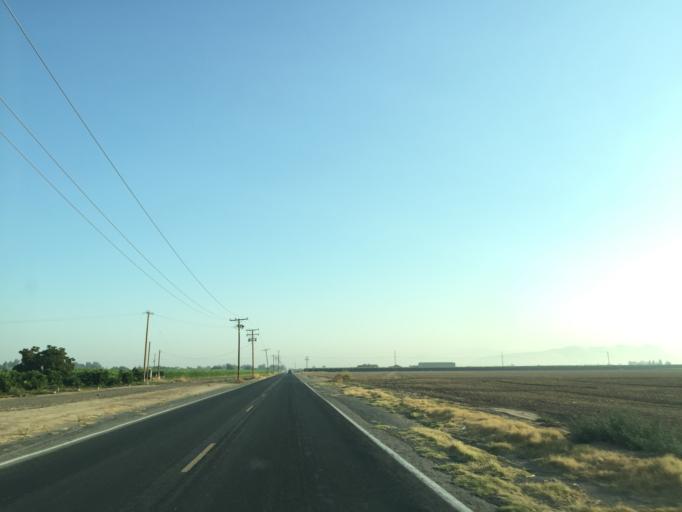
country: US
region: California
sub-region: Tulare County
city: Ivanhoe
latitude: 36.4096
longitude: -119.2782
